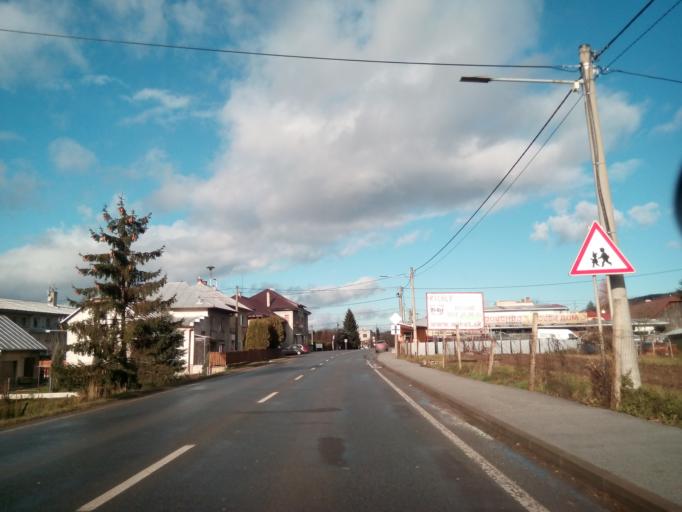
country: SK
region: Presovsky
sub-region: Okres Bardejov
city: Bardejov
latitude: 49.2131
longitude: 21.2973
